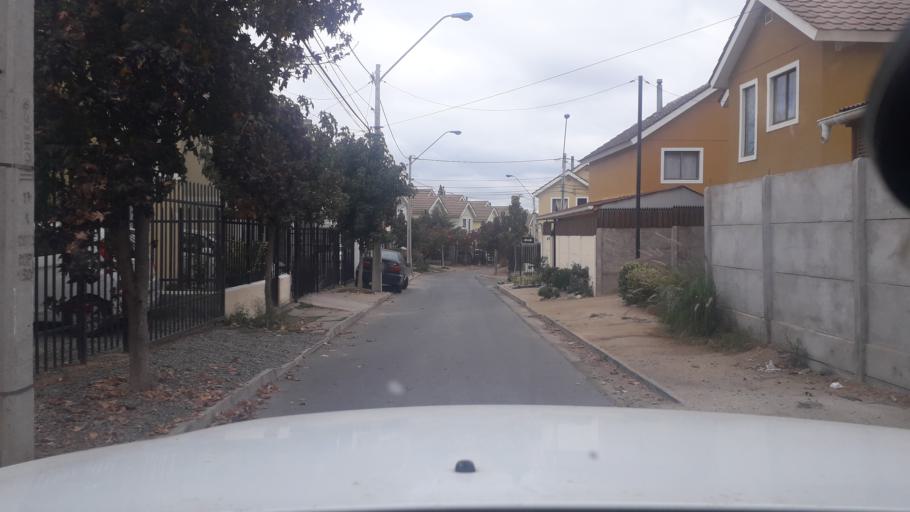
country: CL
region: Valparaiso
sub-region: Provincia de Marga Marga
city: Villa Alemana
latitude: -33.0515
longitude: -71.3332
